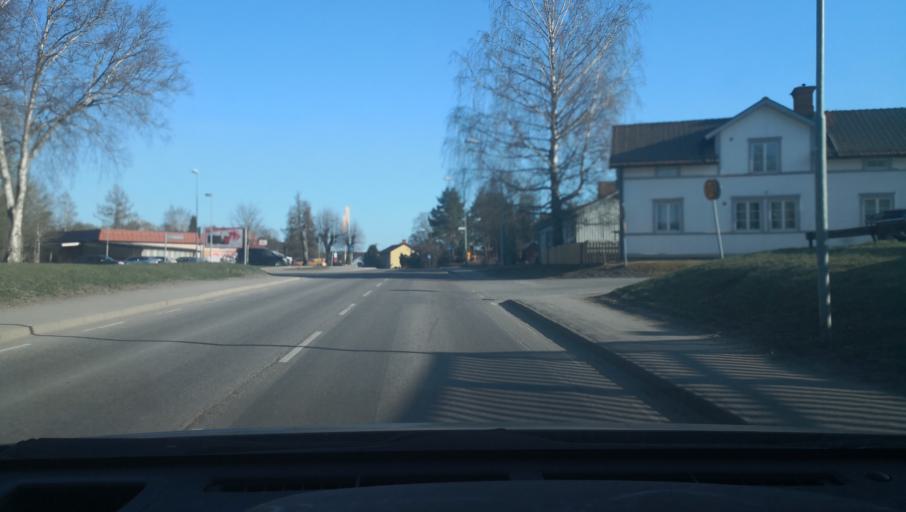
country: SE
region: Uppsala
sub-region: Heby Kommun
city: Heby
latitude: 59.9391
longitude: 16.8647
